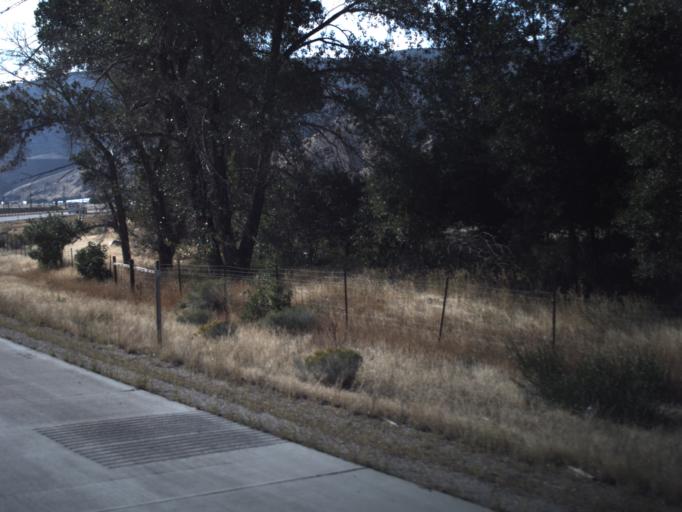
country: US
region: Utah
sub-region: Morgan County
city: Morgan
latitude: 41.0490
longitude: -111.6078
